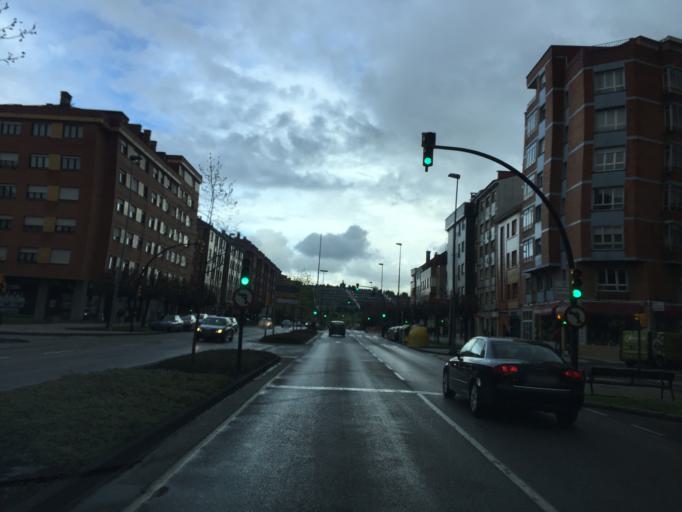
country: ES
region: Asturias
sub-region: Province of Asturias
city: Gijon
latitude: 43.5259
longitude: -5.6686
